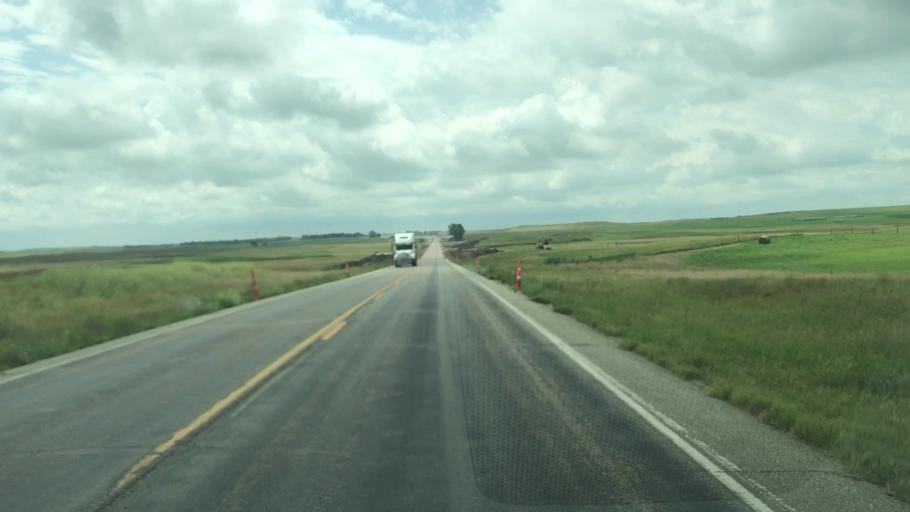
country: US
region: Nebraska
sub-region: Cherry County
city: Valentine
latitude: 43.0568
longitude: -100.5948
